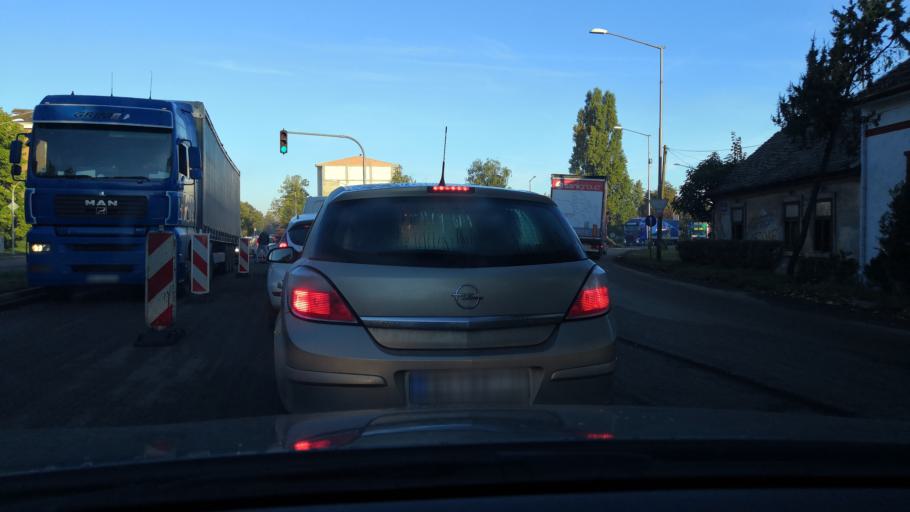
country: RS
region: Autonomna Pokrajina Vojvodina
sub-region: Juznobacki Okrug
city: Petrovaradin
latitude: 45.2484
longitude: 19.8775
